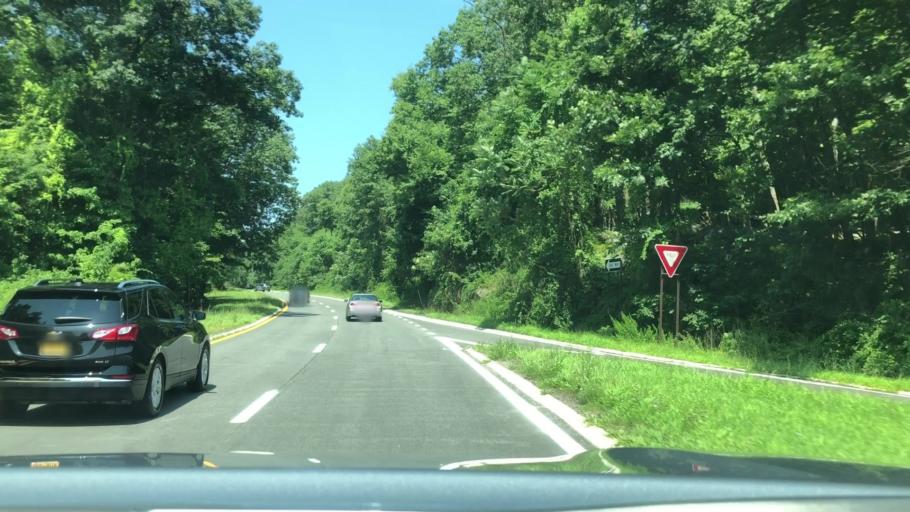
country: US
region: New York
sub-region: Rockland County
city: Thiells
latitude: 41.2460
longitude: -74.0308
